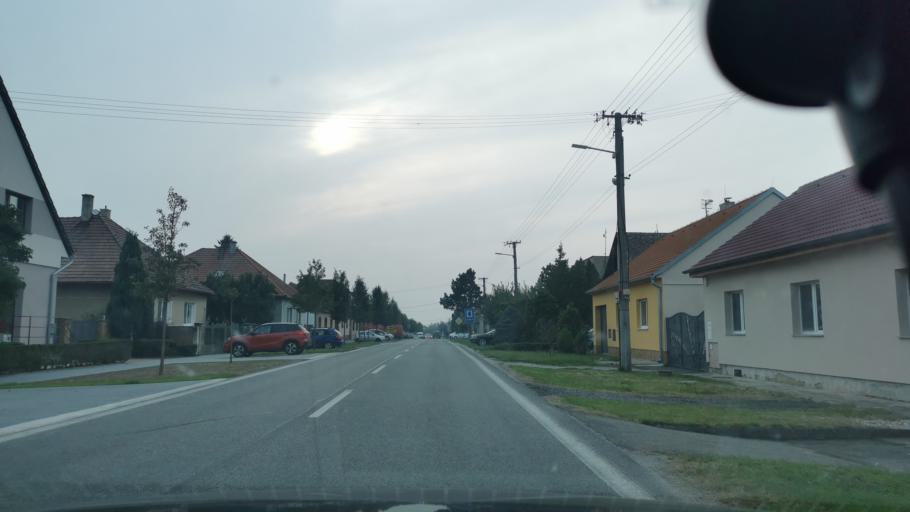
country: SK
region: Trnavsky
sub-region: Okres Skalica
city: Holic
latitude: 48.7920
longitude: 17.1280
